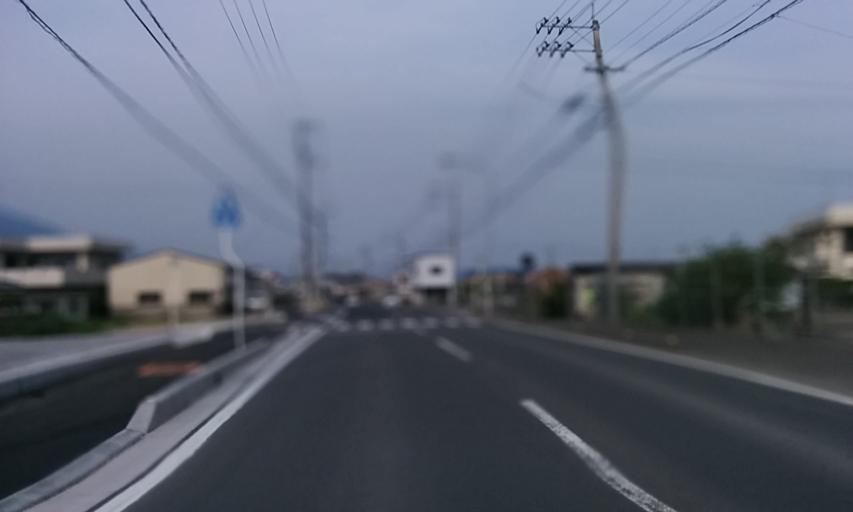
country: JP
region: Ehime
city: Kawanoecho
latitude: 33.9670
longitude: 133.4775
